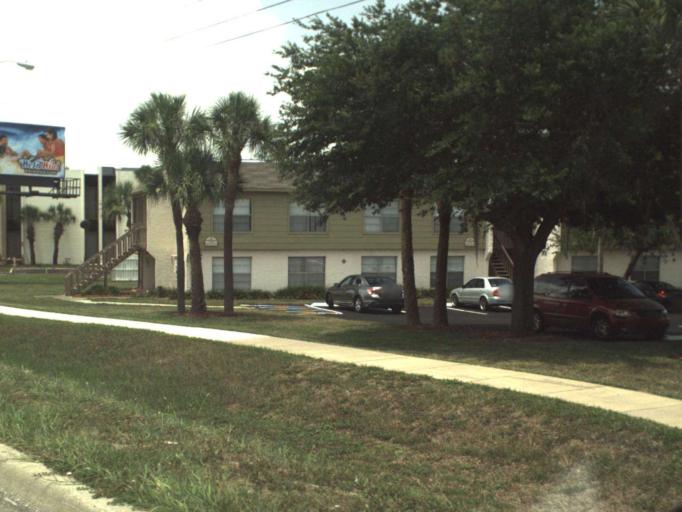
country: US
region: Florida
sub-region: Seminole County
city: Goldenrod
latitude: 28.6282
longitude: -81.3170
